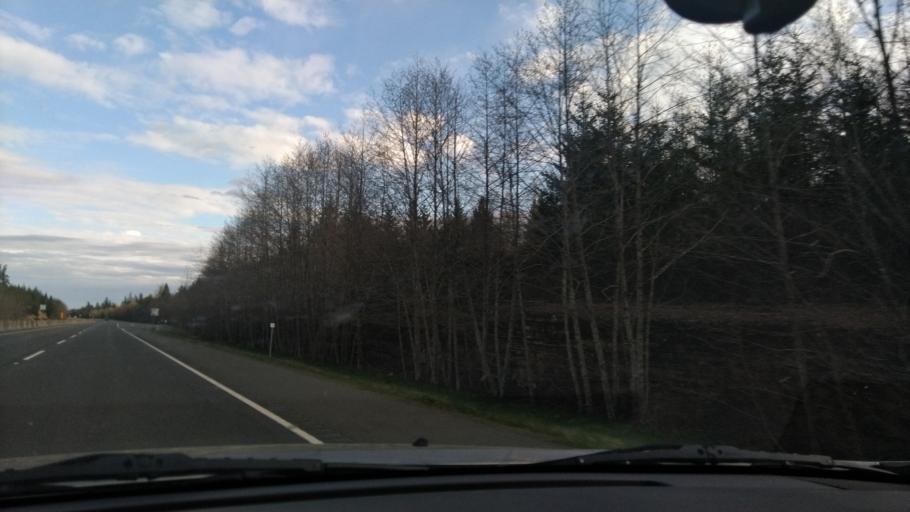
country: CA
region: British Columbia
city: Courtenay
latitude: 49.7442
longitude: -125.1207
